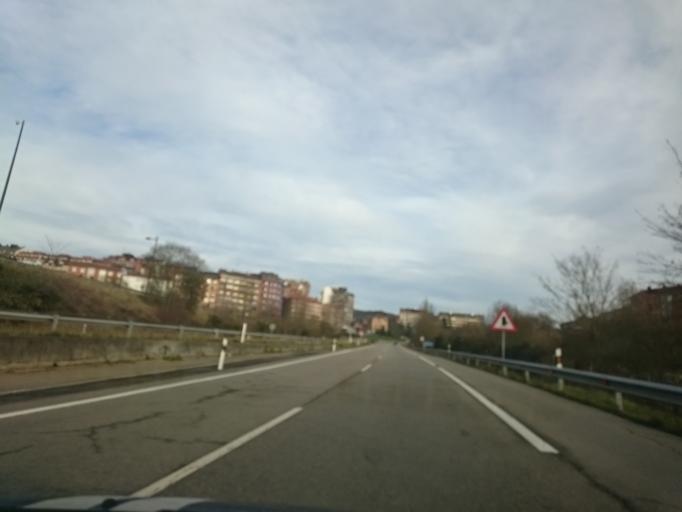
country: ES
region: Asturias
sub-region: Province of Asturias
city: Oviedo
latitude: 43.3510
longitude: -5.8564
